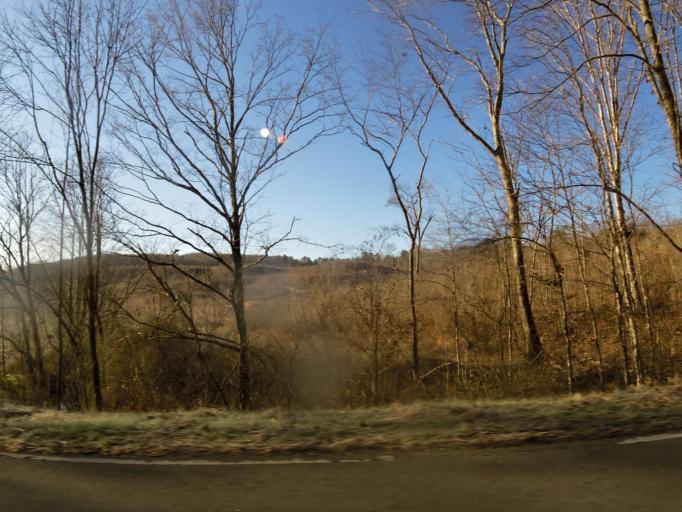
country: US
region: Alabama
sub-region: Morgan County
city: Falkville
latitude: 34.3098
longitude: -86.8965
